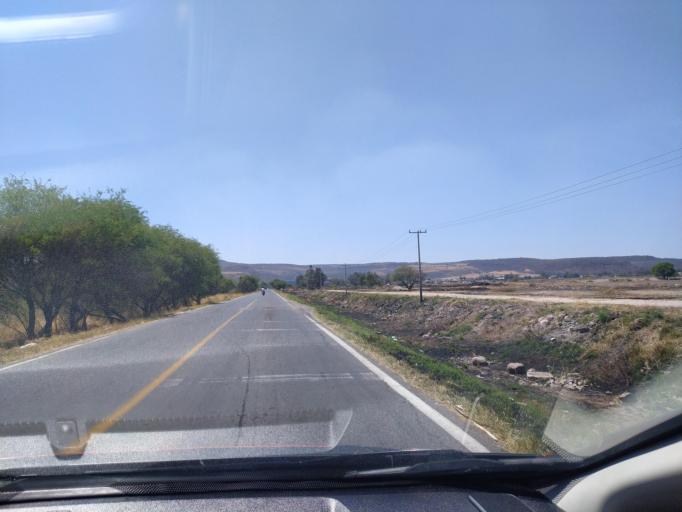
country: MX
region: Guanajuato
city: Ciudad Manuel Doblado
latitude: 20.7409
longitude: -101.9416
